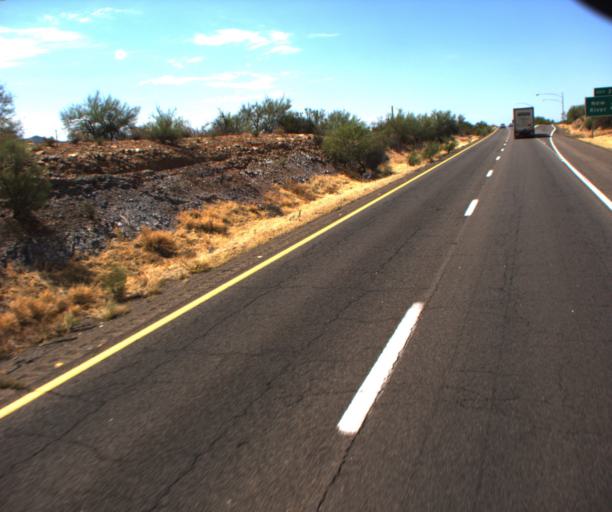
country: US
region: Arizona
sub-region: Maricopa County
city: New River
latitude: 33.9179
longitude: -112.1452
